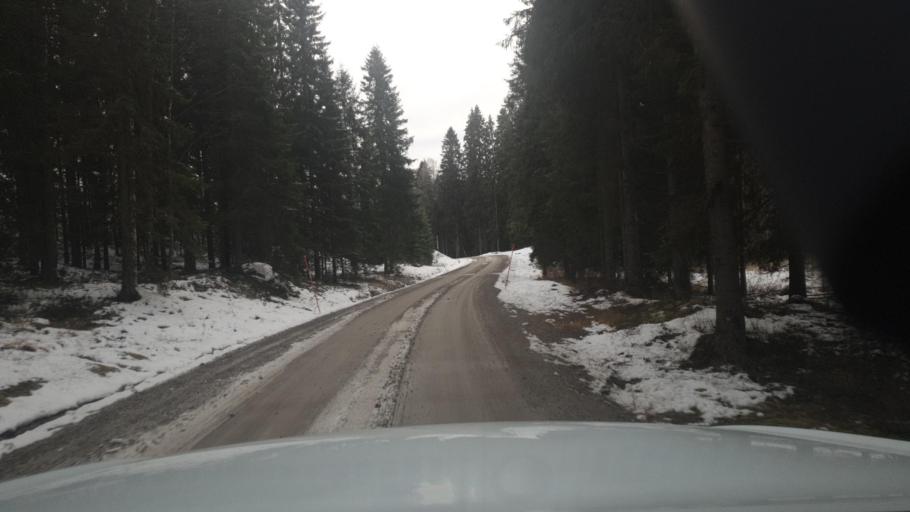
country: SE
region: Vaermland
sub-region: Sunne Kommun
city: Sunne
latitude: 59.8560
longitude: 12.8464
